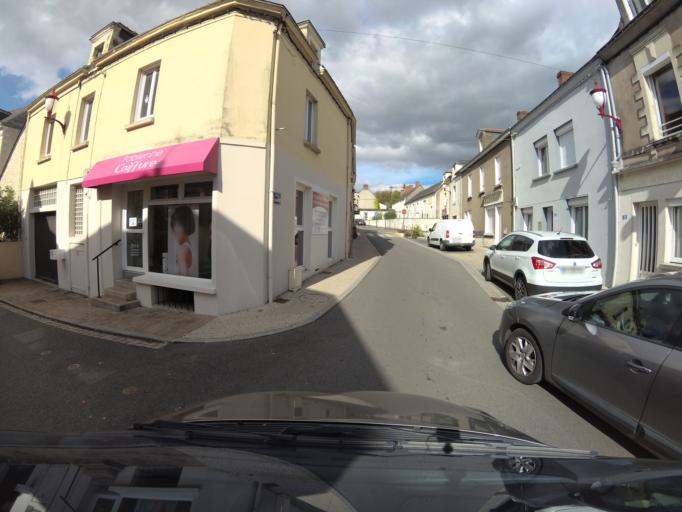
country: FR
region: Pays de la Loire
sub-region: Departement de la Loire-Atlantique
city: Suce-sur-Erdre
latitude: 47.3409
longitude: -1.5263
